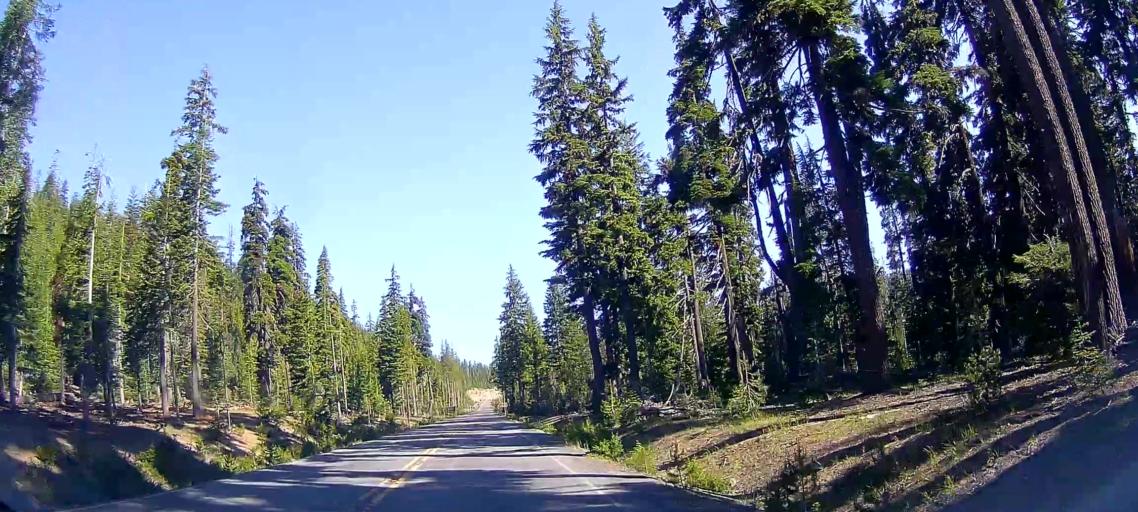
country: US
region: Oregon
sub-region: Jackson County
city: Shady Cove
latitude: 42.8622
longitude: -122.1664
